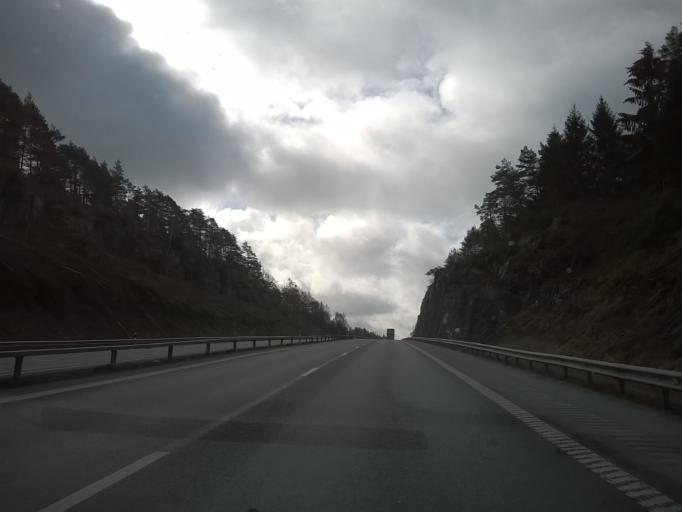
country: SE
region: Halland
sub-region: Kungsbacka Kommun
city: Frillesas
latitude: 57.3129
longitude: 12.2114
